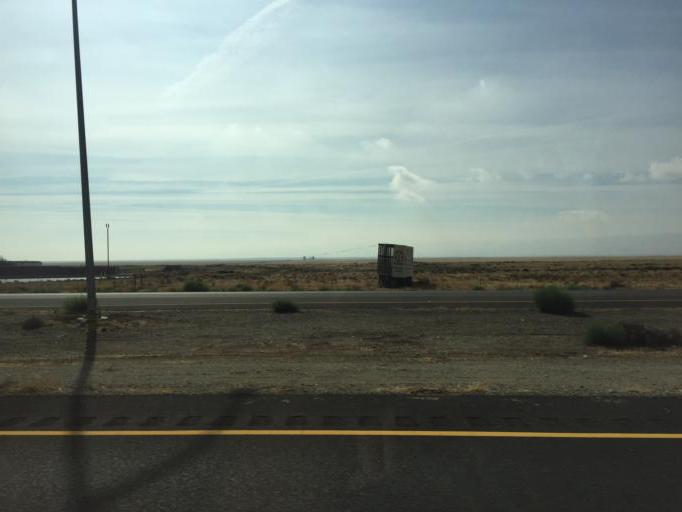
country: US
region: California
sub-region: Kern County
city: Lost Hills
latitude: 35.6152
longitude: -119.8702
